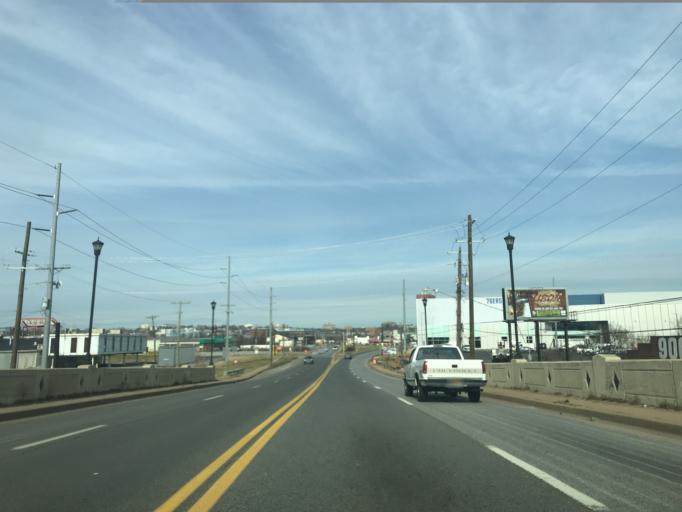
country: US
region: Delaware
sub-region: New Castle County
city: Wilmington
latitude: 39.7255
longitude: -75.5558
